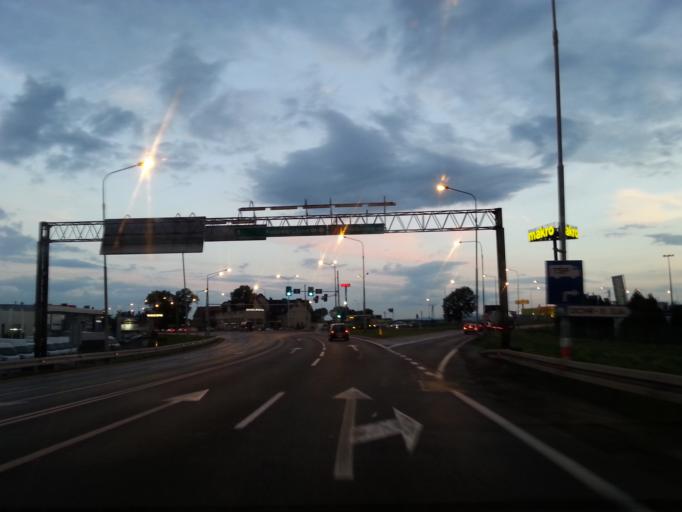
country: PL
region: Lower Silesian Voivodeship
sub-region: Powiat wroclawski
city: Bielany Wroclawskie
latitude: 51.0482
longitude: 16.9712
